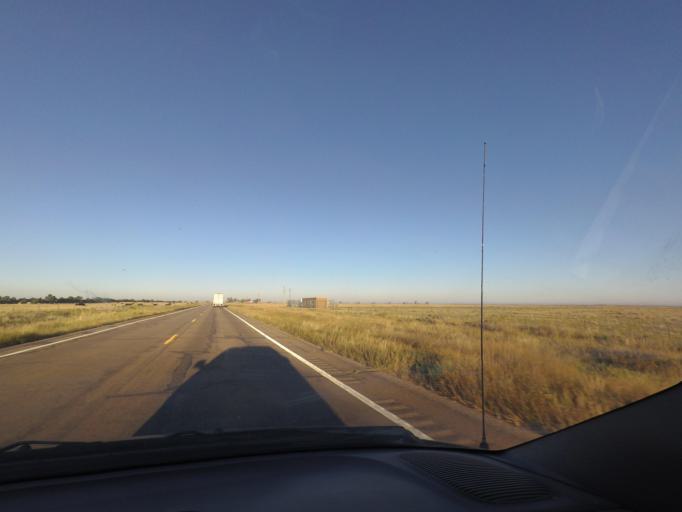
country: US
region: Colorado
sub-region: Yuma County
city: Yuma
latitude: 39.6703
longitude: -102.8760
